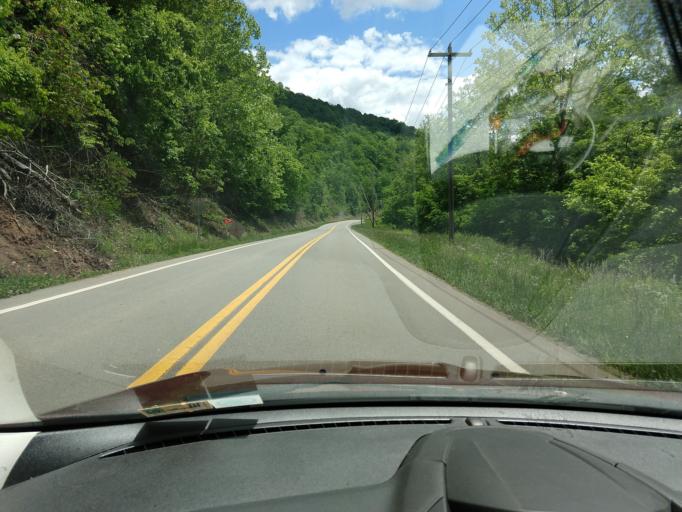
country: US
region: West Virginia
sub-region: Gilmer County
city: Glenville
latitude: 38.8896
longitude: -80.7243
